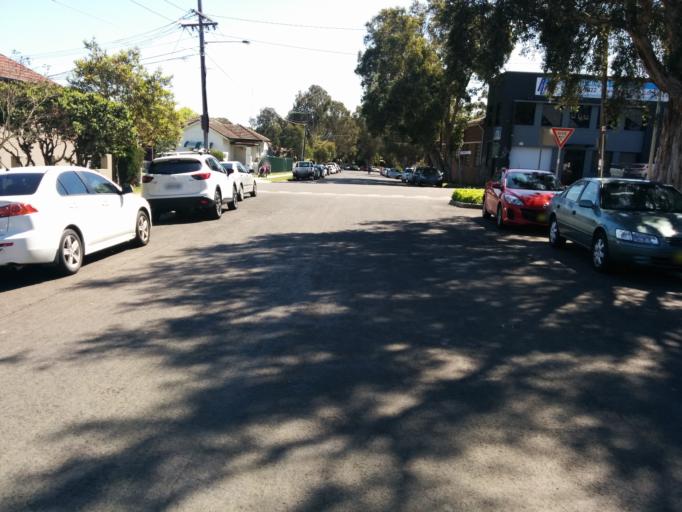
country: AU
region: New South Wales
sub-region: Canada Bay
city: Concord West
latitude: -33.8482
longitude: 151.0851
